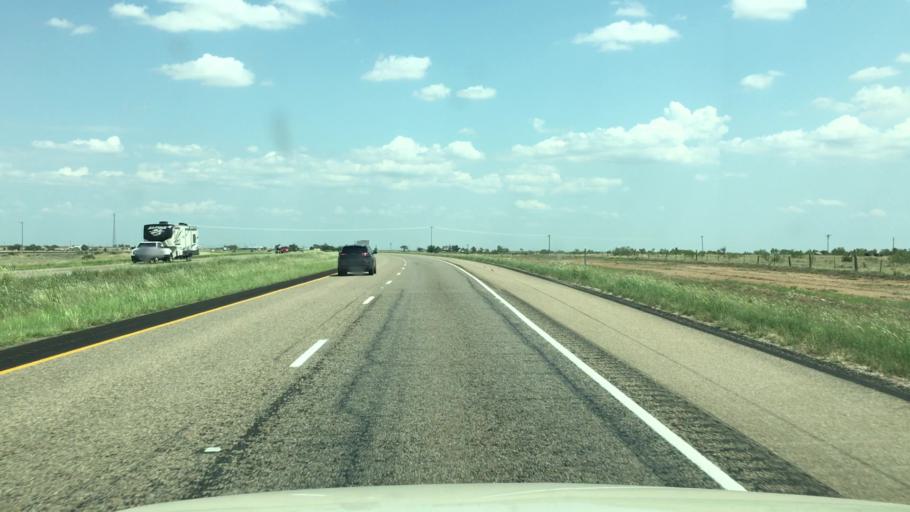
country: US
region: Texas
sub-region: Armstrong County
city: Claude
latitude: 35.0352
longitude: -101.1985
